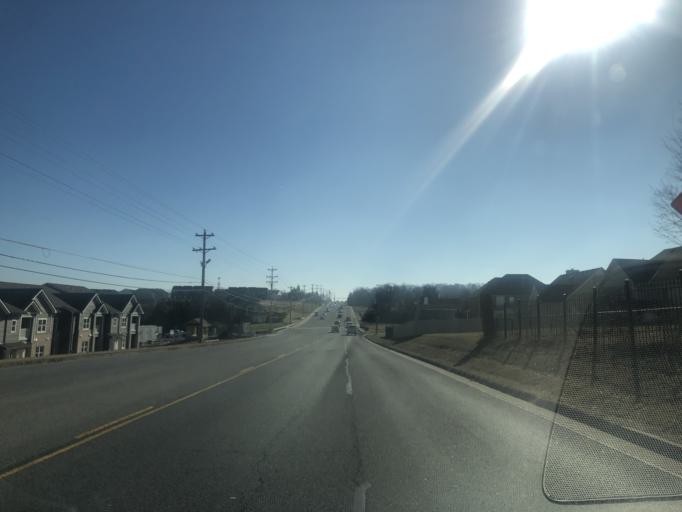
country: US
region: Tennessee
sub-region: Rutherford County
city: Smyrna
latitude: 35.9782
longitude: -86.5401
